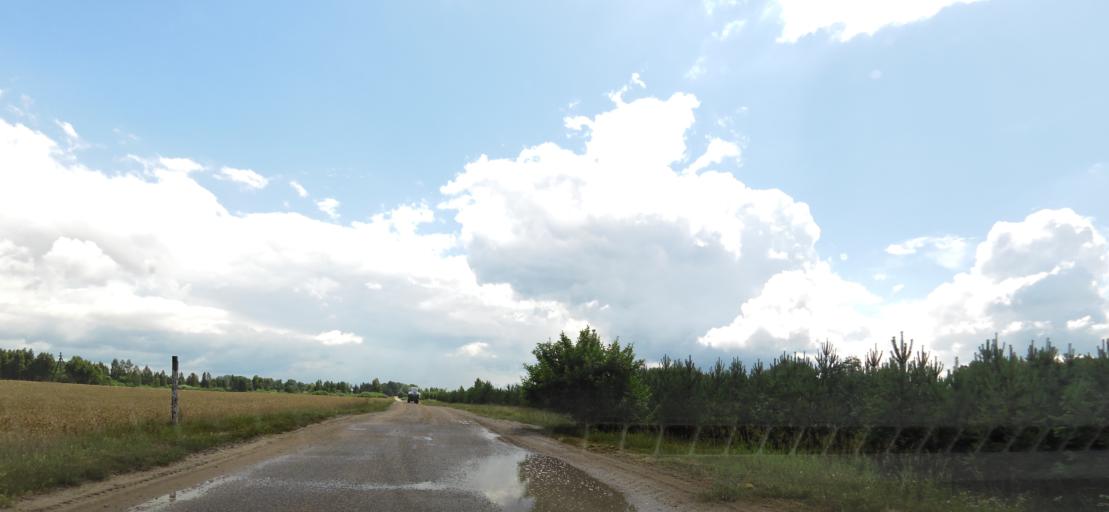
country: LT
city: Vabalninkas
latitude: 55.8859
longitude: 24.7702
